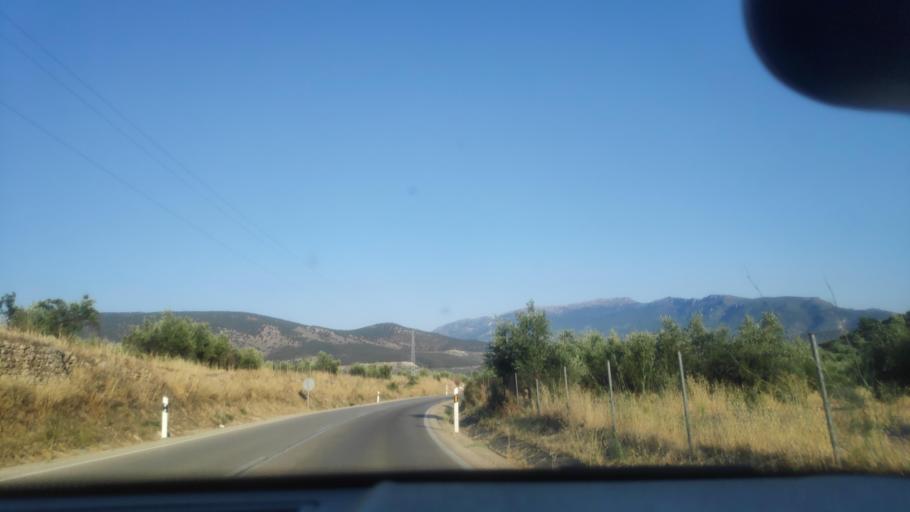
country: ES
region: Andalusia
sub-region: Provincia de Jaen
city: Jaen
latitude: 37.7463
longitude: -3.7798
